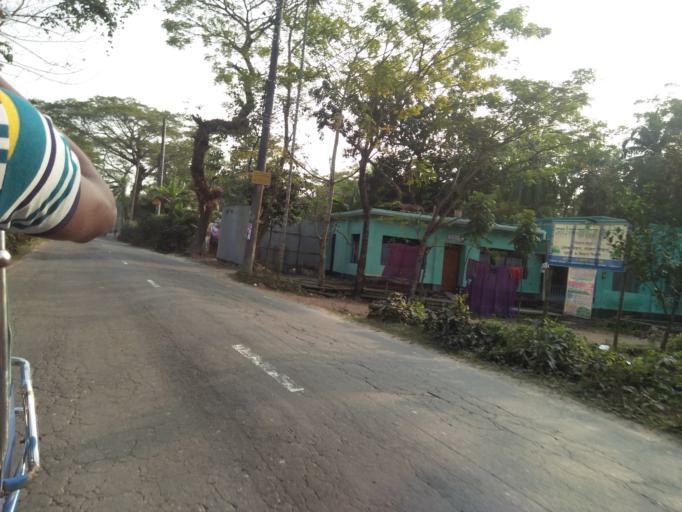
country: BD
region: Barisal
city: Bhola
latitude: 22.6991
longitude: 90.6426
